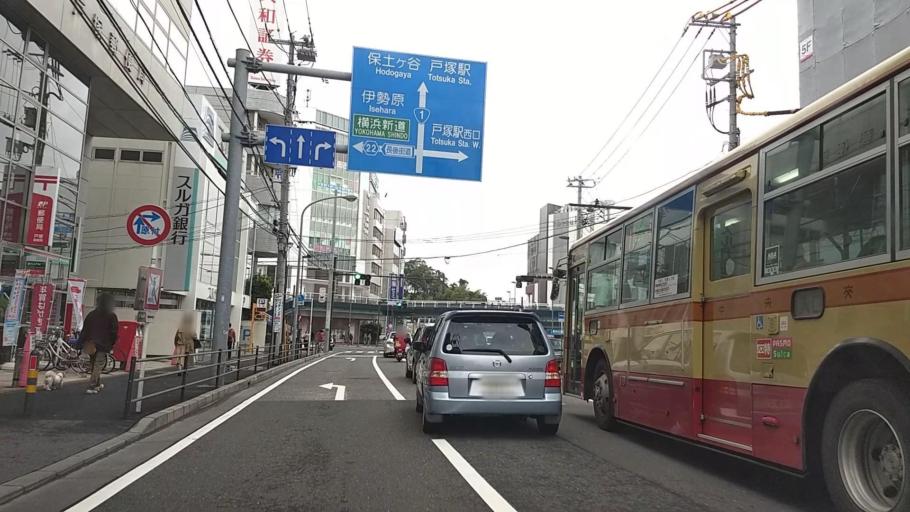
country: JP
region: Kanagawa
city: Fujisawa
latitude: 35.3997
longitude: 139.5313
